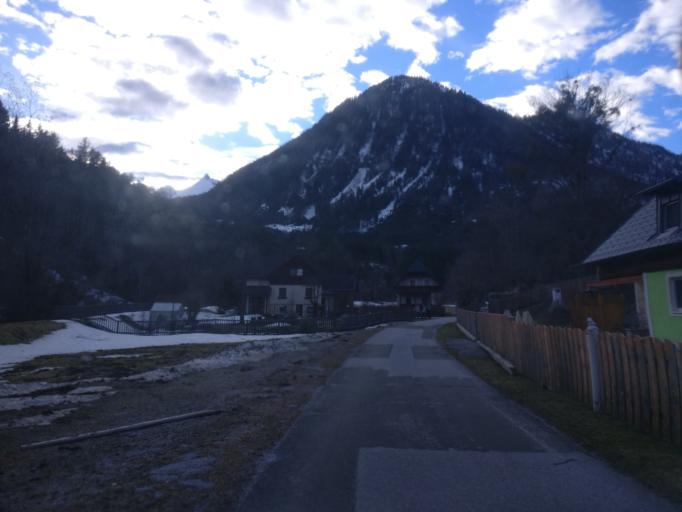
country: AT
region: Styria
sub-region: Politischer Bezirk Liezen
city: Sankt Martin am Grimming
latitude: 47.4888
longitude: 13.9645
